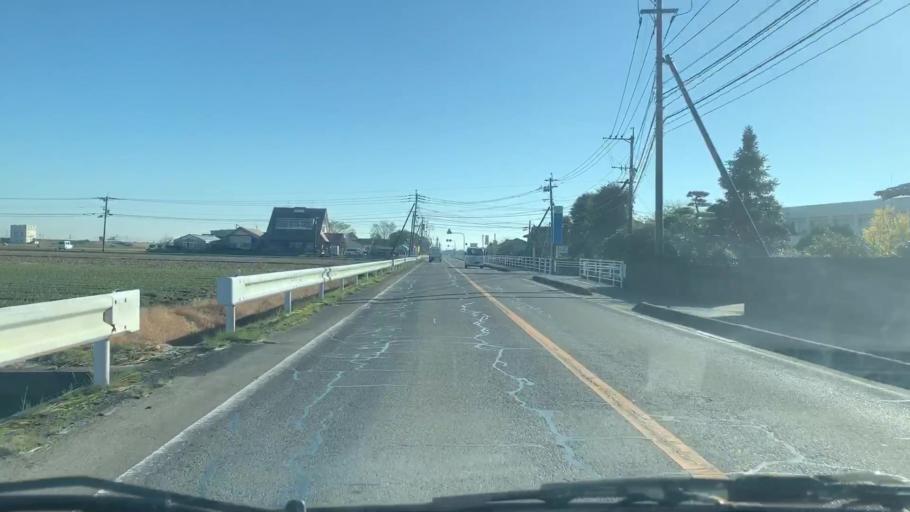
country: JP
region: Saga Prefecture
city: Kashima
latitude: 33.1857
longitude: 130.1496
